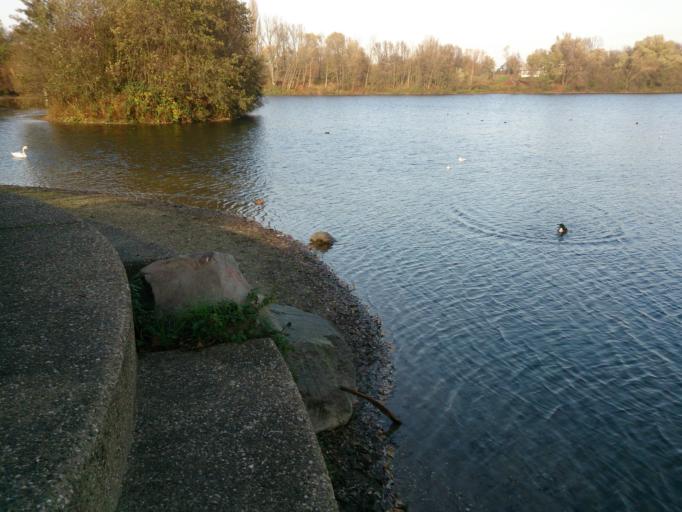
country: DE
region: North Rhine-Westphalia
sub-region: Regierungsbezirk Dusseldorf
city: Dusseldorf
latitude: 51.1956
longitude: 6.8069
